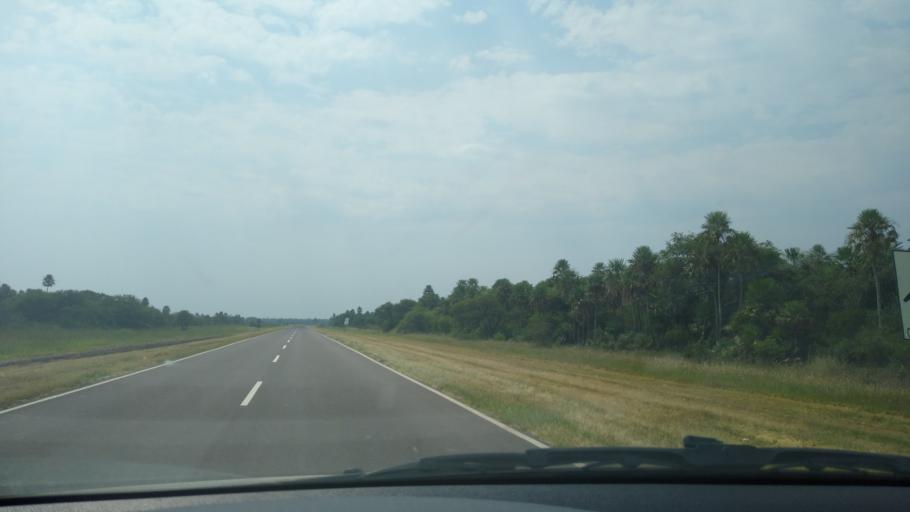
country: AR
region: Chaco
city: Margarita Belen
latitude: -27.0799
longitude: -58.9606
